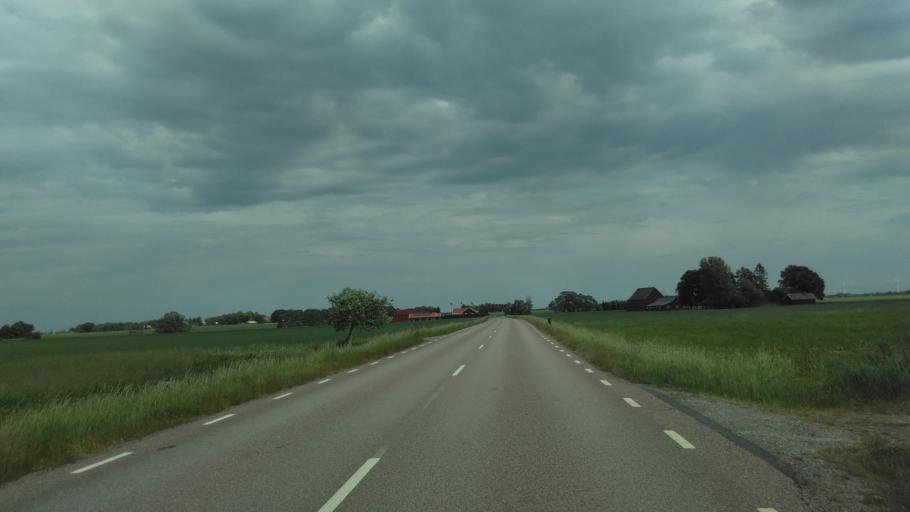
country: SE
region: Vaestra Goetaland
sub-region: Vara Kommun
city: Kvanum
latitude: 58.3602
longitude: 13.1403
